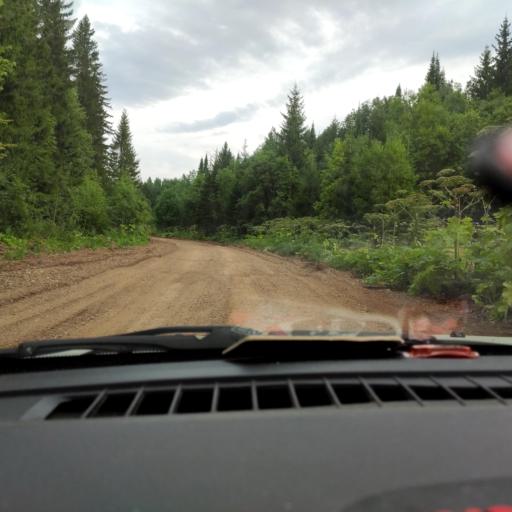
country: RU
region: Perm
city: Kultayevo
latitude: 57.8149
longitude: 56.0011
